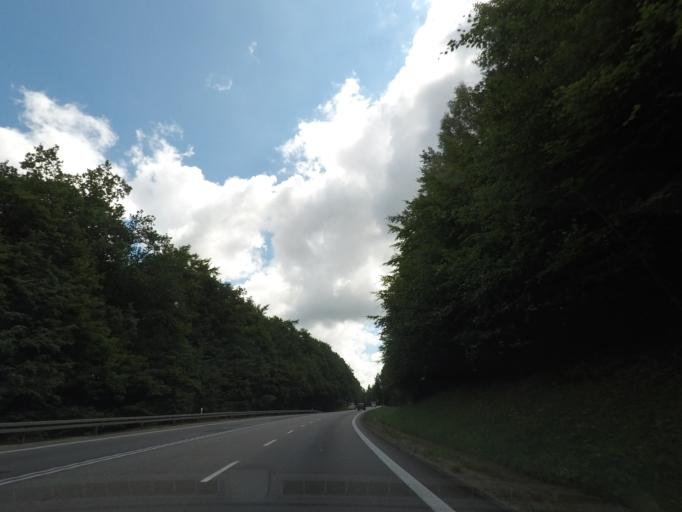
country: PL
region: Pomeranian Voivodeship
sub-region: Powiat wejherowski
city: Luzino
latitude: 54.5814
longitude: 18.0873
